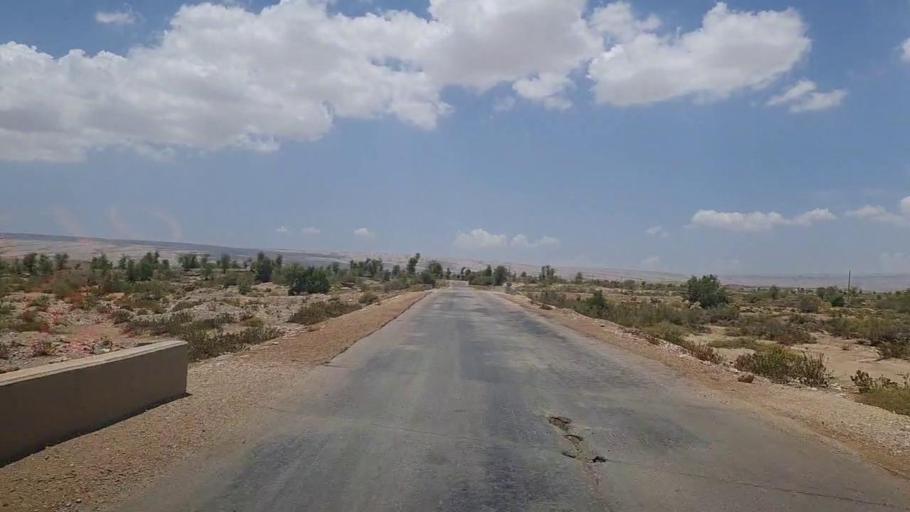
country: PK
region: Sindh
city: Sehwan
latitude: 26.3207
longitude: 67.6518
